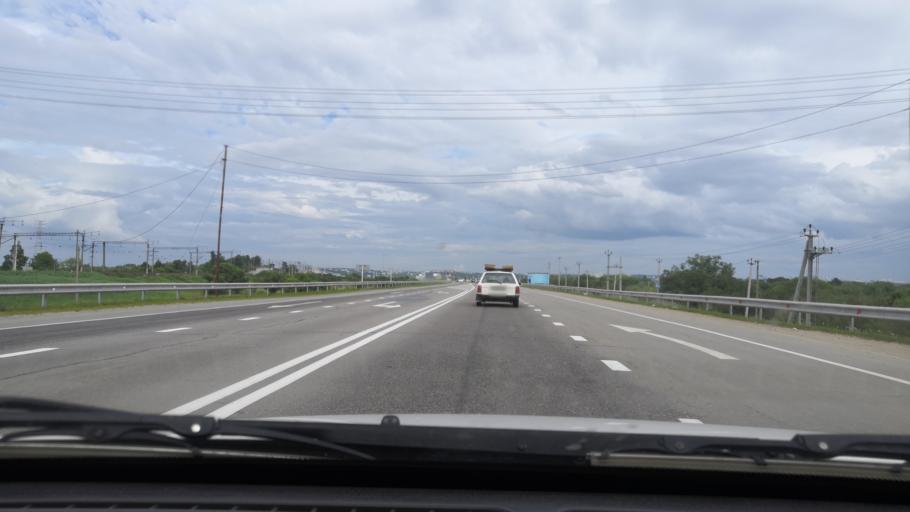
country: RU
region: Jewish Autonomous Oblast
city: Priamurskiy
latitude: 48.5269
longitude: 134.9502
